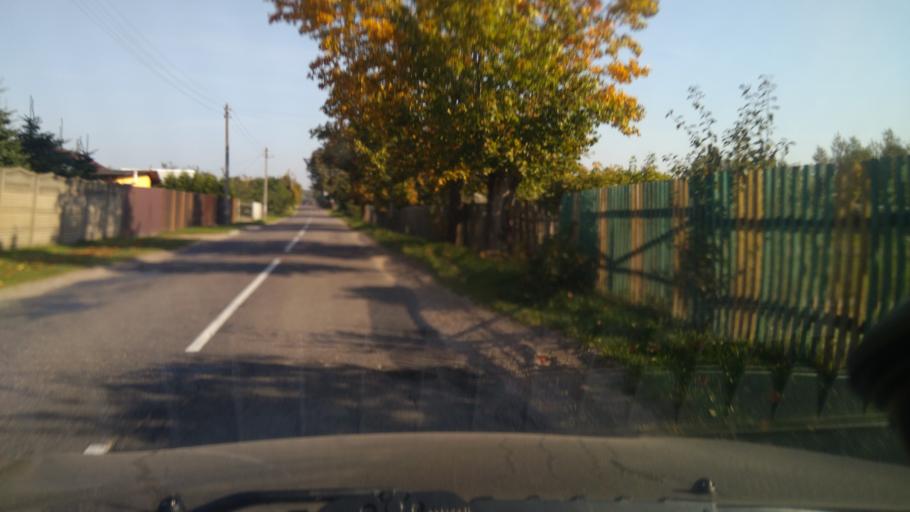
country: BY
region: Minsk
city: Rakaw
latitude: 54.0042
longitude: 27.0467
